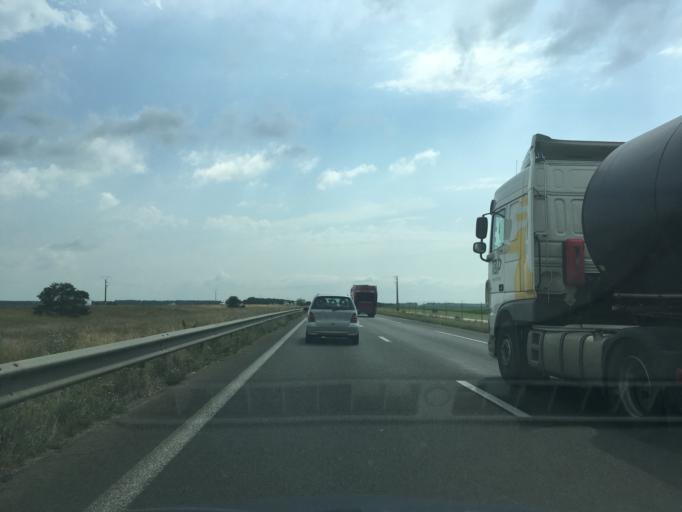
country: FR
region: Aquitaine
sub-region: Departement de la Gironde
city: Saint-Aubin-de-Medoc
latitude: 44.6976
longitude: -0.7627
